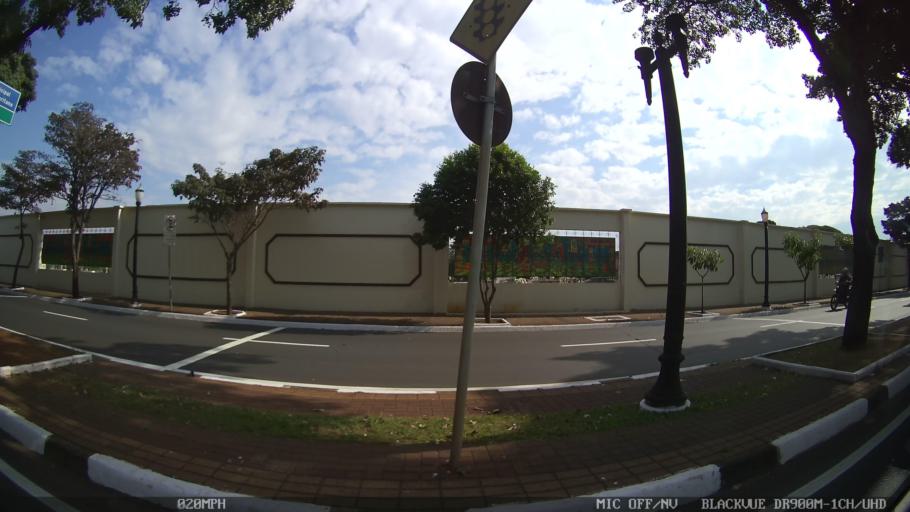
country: BR
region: Sao Paulo
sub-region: Paulinia
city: Paulinia
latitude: -22.7695
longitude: -47.1477
